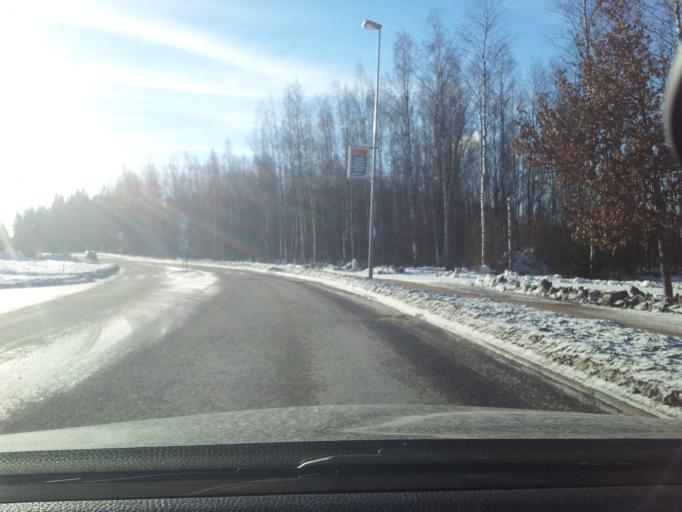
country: FI
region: Uusimaa
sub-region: Helsinki
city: Koukkuniemi
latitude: 60.1587
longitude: 24.7255
